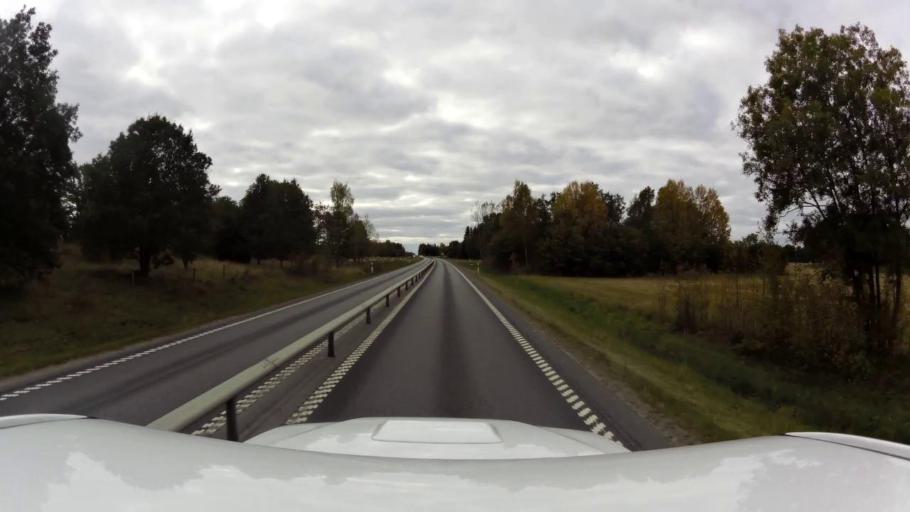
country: SE
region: OEstergoetland
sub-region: Linkopings Kommun
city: Malmslatt
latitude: 58.3640
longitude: 15.5446
